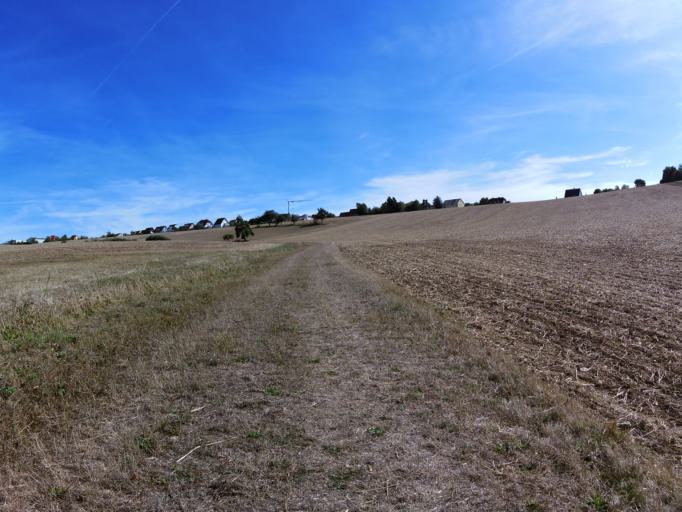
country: DE
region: Bavaria
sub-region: Regierungsbezirk Unterfranken
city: Eisingen
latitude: 49.7650
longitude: 9.8314
